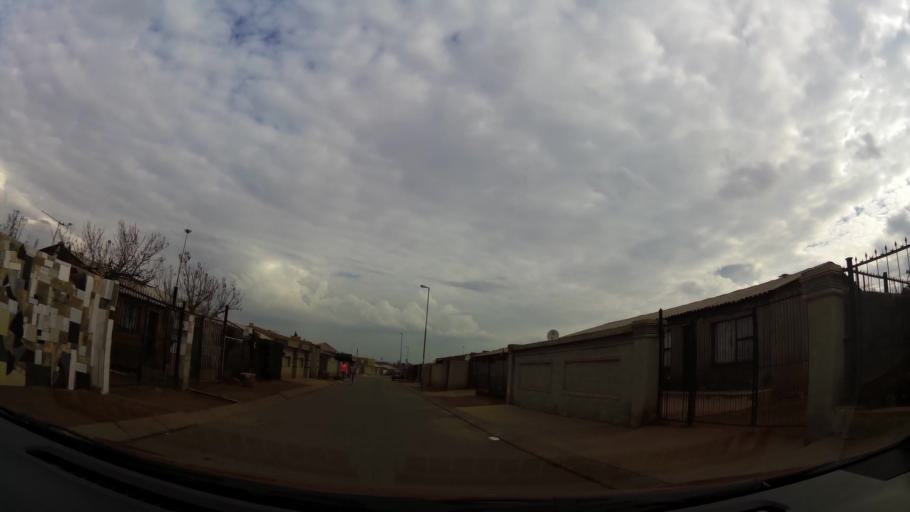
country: ZA
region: Gauteng
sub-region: City of Johannesburg Metropolitan Municipality
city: Soweto
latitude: -26.2446
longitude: 27.8388
